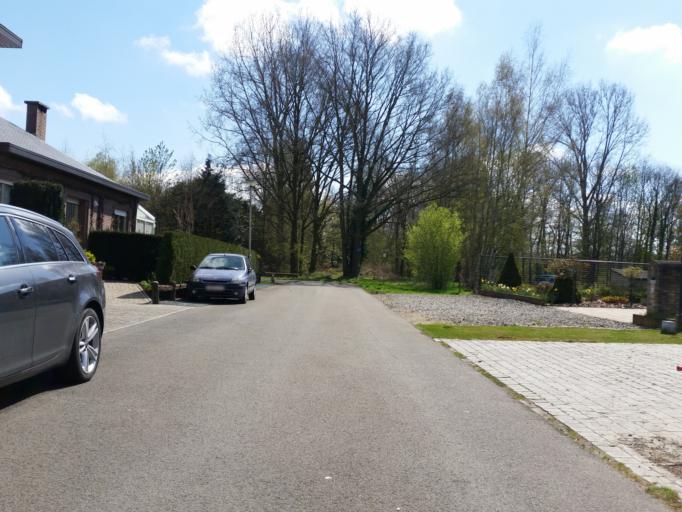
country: BE
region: Flanders
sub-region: Provincie Vlaams-Brabant
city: Boortmeerbeek
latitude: 50.9808
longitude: 4.5340
